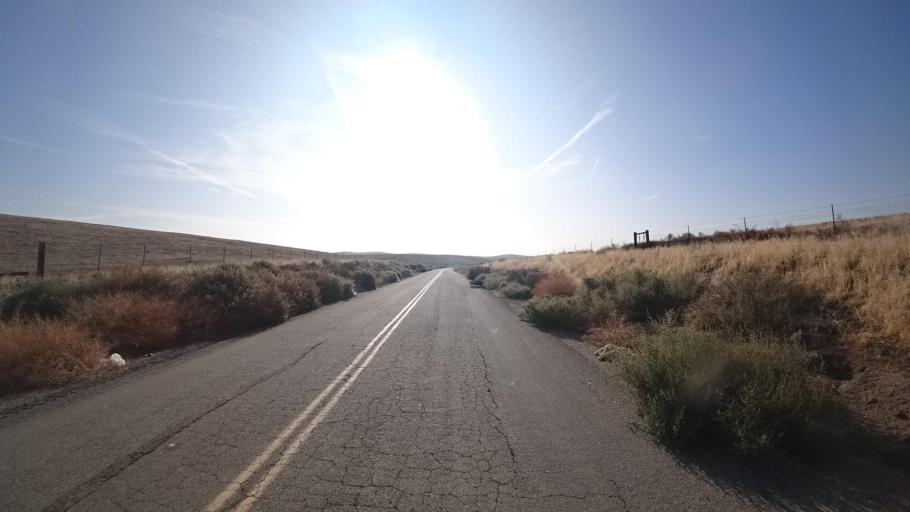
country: US
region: California
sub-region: Tulare County
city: Richgrove
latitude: 35.6292
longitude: -119.0322
